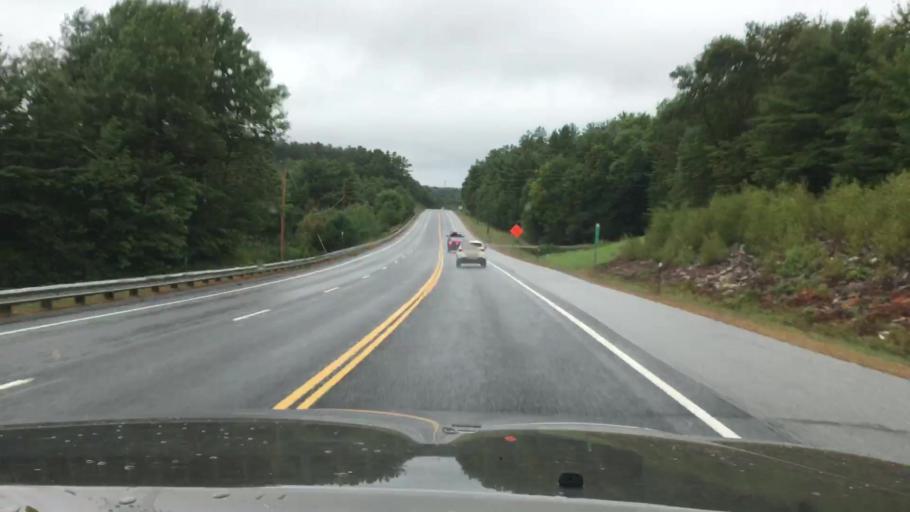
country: US
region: New Hampshire
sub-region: Cheshire County
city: Harrisville
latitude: 43.0043
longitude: -72.1751
